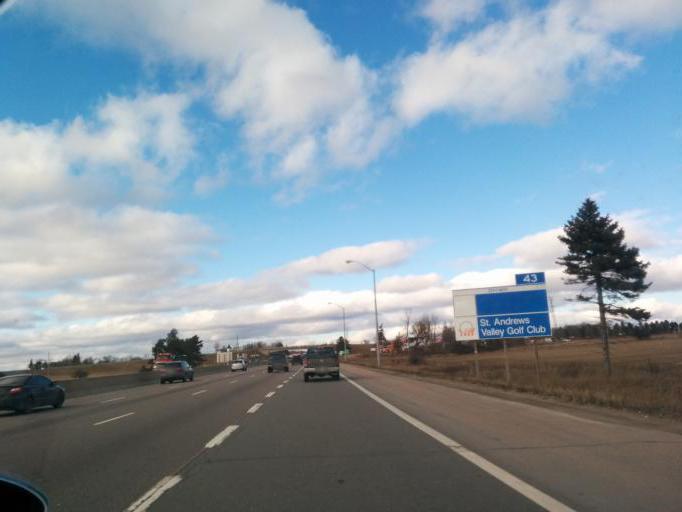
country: CA
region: Ontario
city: Vaughan
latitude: 43.8985
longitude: -79.5607
